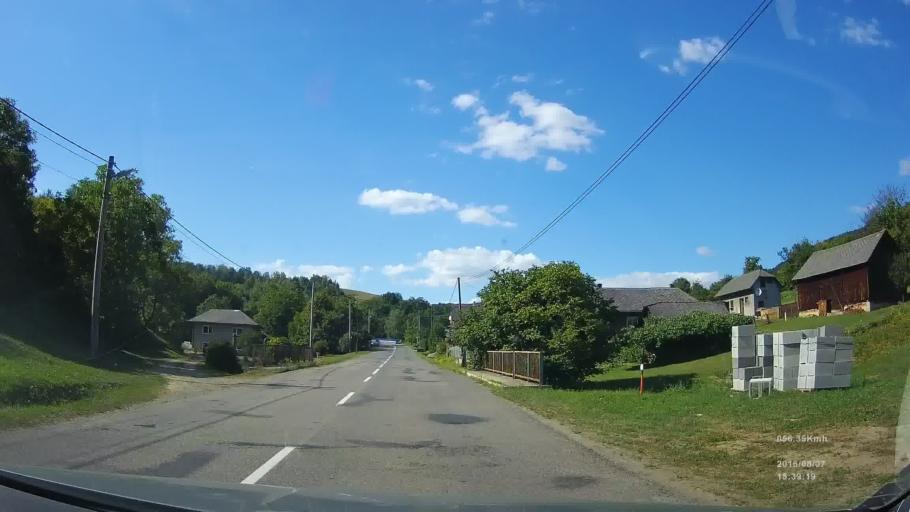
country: SK
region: Presovsky
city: Giraltovce
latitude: 49.1172
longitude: 21.6046
